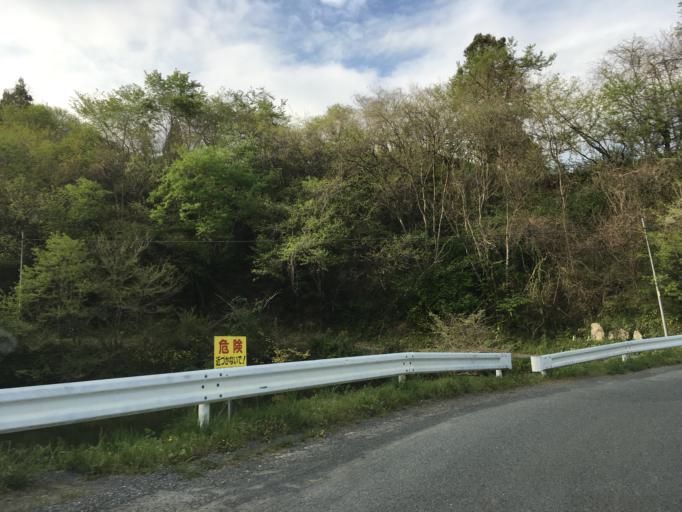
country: JP
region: Iwate
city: Ichinoseki
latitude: 38.9124
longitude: 141.2197
